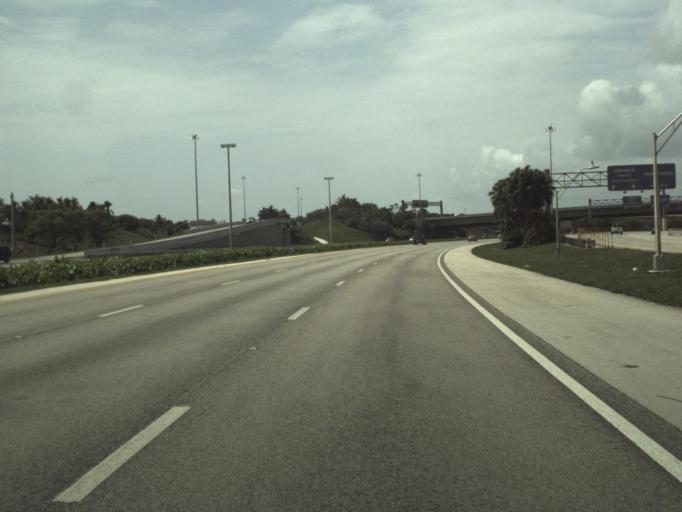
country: US
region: Florida
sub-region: Broward County
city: Dania Beach
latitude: 26.0757
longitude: -80.1337
